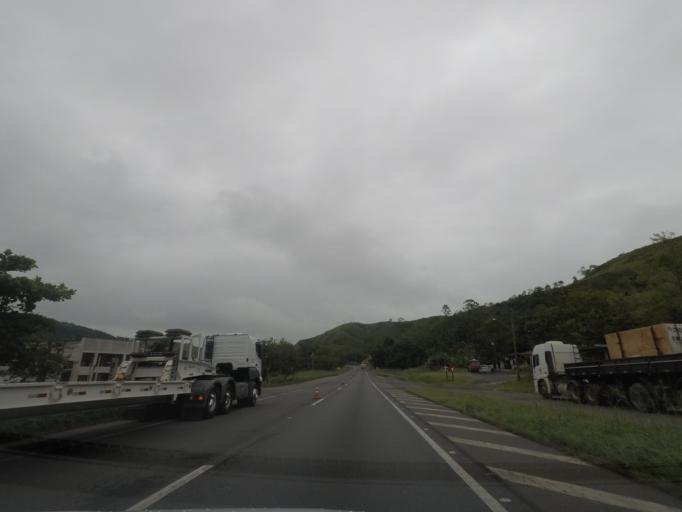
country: BR
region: Sao Paulo
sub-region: Cajati
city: Cajati
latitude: -24.8048
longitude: -48.2120
